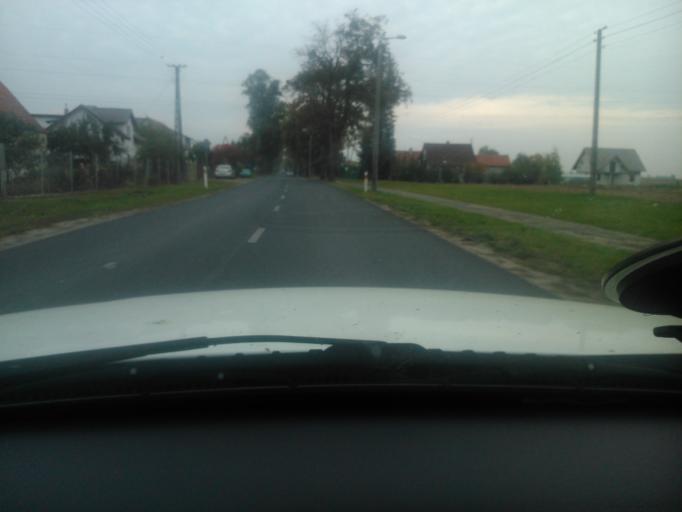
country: PL
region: Kujawsko-Pomorskie
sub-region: Powiat golubsko-dobrzynski
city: Kowalewo Pomorskie
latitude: 53.1616
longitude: 18.8769
